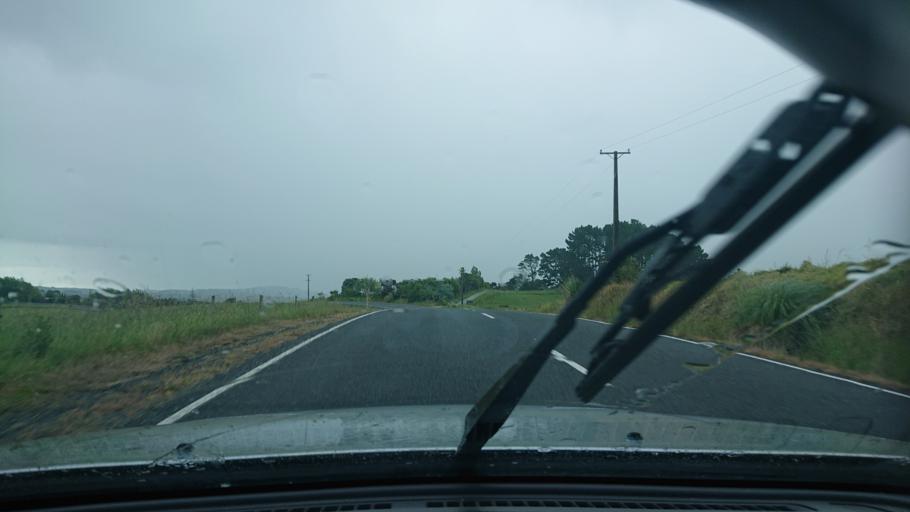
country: NZ
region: Auckland
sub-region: Auckland
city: Wellsford
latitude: -36.3336
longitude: 174.3943
